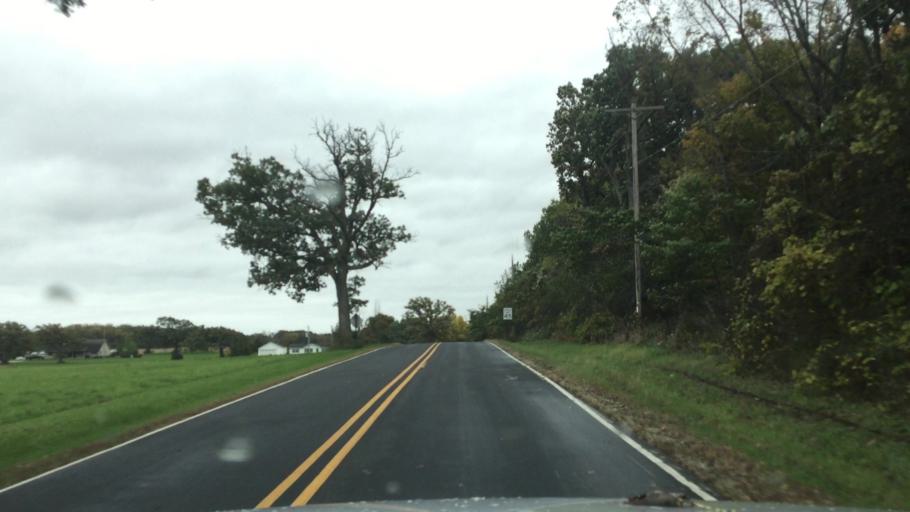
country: US
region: Wisconsin
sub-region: Racine County
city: Waterford
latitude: 42.7596
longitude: -88.1606
